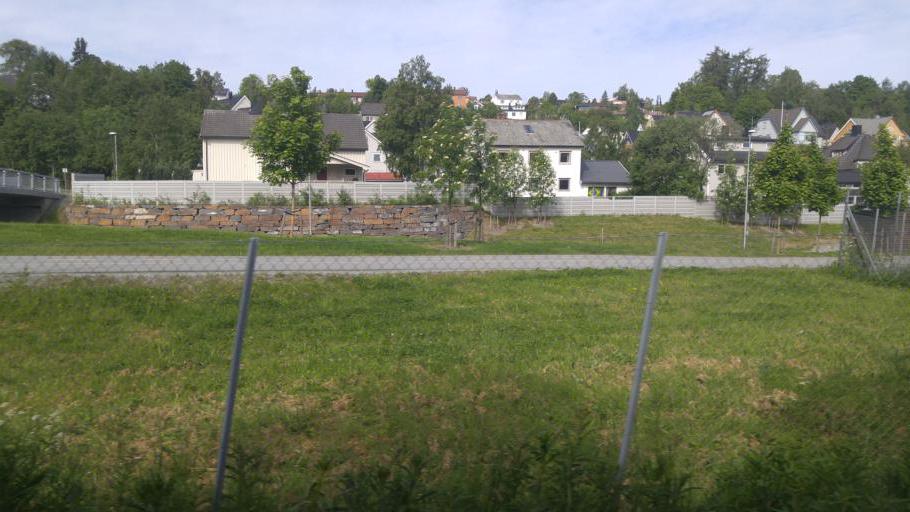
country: NO
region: Sor-Trondelag
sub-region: Trondheim
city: Trondheim
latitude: 63.4131
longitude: 10.3839
